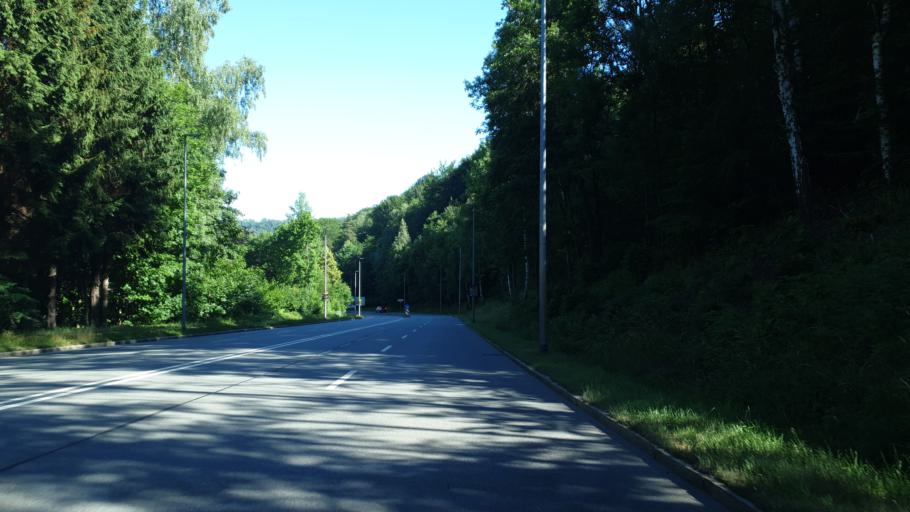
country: DE
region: Saxony
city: Schlema
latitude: 50.5945
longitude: 12.6853
